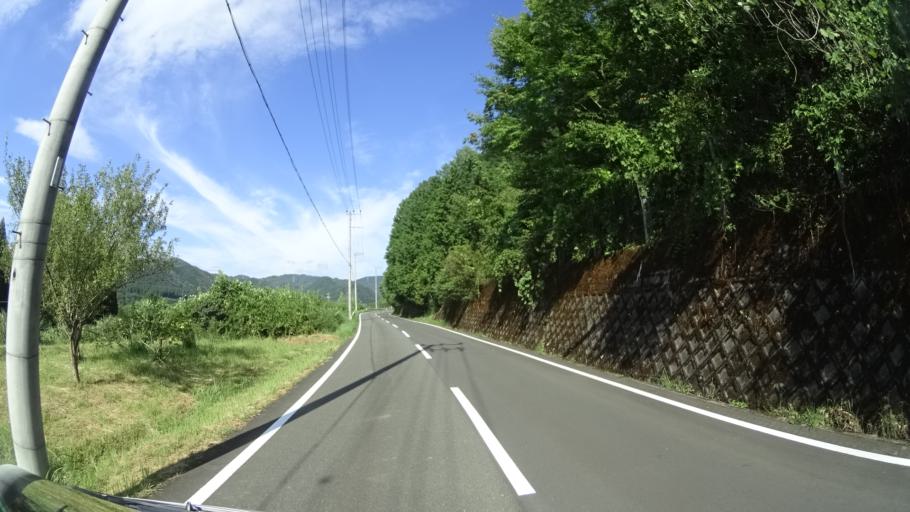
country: JP
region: Kyoto
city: Ayabe
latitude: 35.2905
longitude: 135.3134
